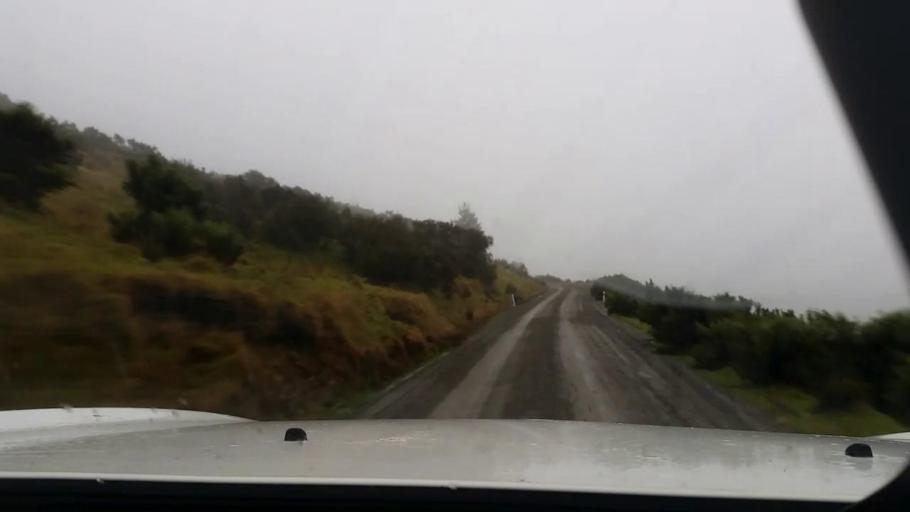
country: NZ
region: Wellington
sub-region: Masterton District
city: Masterton
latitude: -41.2464
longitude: 175.8780
